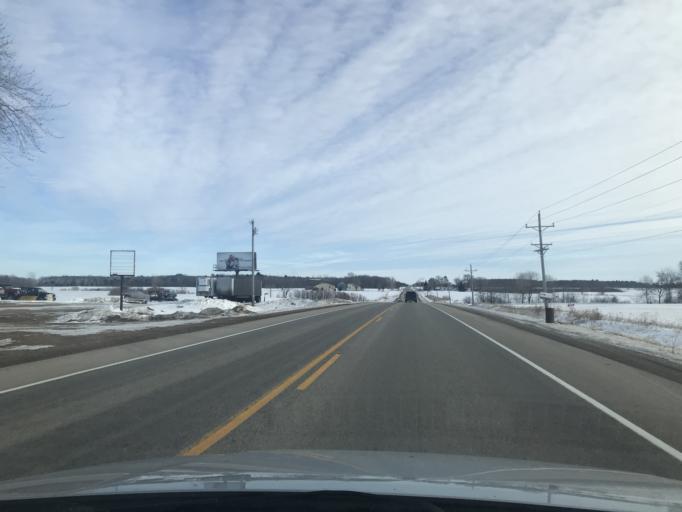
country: US
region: Wisconsin
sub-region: Oconto County
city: Oconto Falls
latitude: 44.8956
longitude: -88.2200
